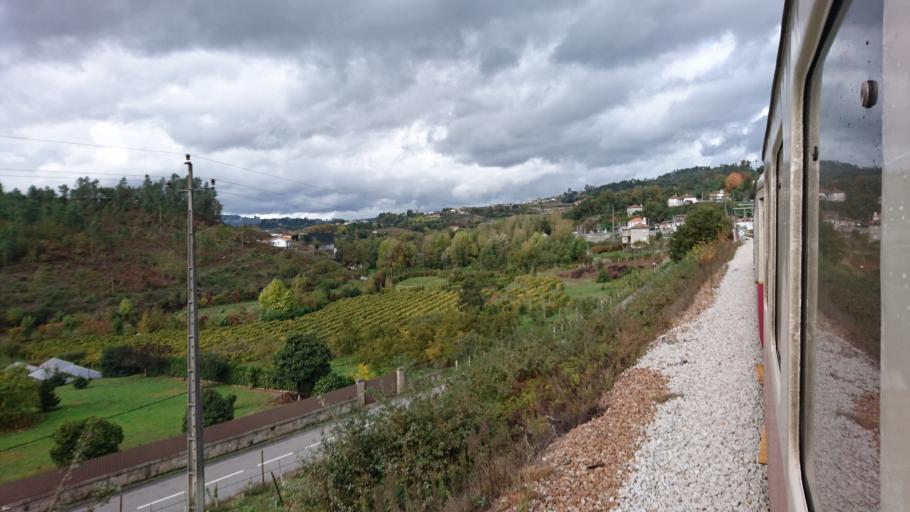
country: PT
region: Porto
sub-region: Marco de Canaveses
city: Marco de Canavezes
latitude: 41.2138
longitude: -8.1540
